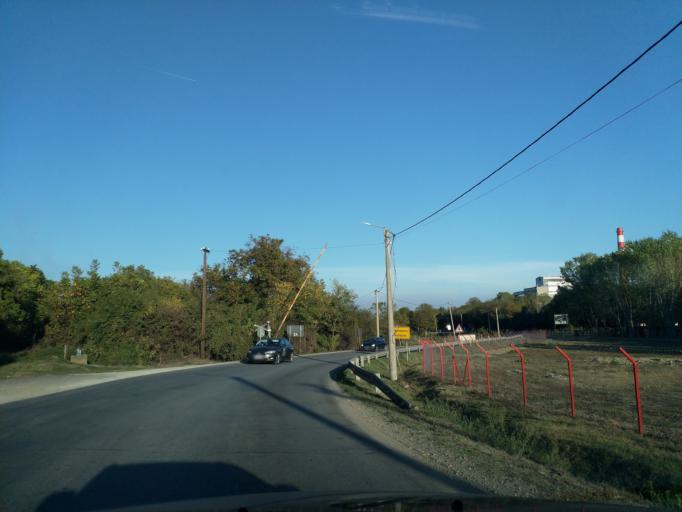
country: RS
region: Central Serbia
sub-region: Pomoravski Okrug
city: Svilajnac
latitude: 44.2256
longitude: 21.1552
